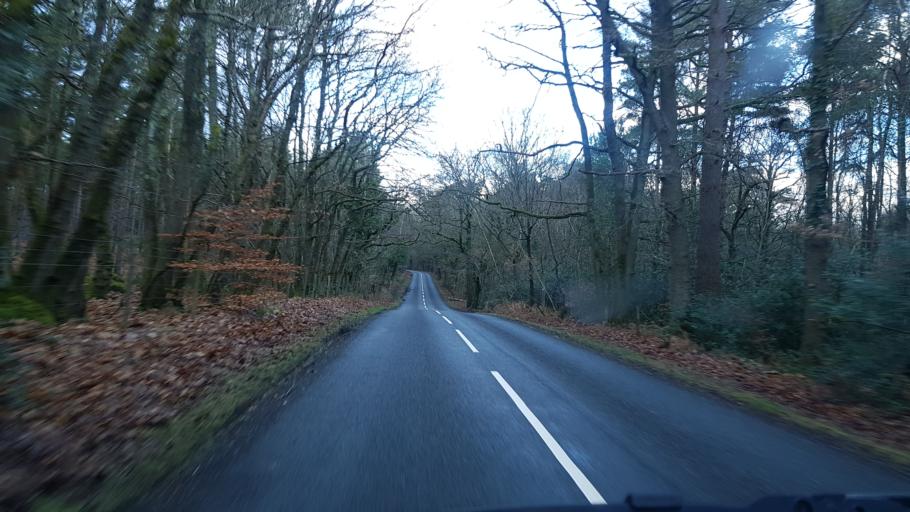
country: GB
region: England
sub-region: Surrey
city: Elstead
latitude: 51.1954
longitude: -0.7162
